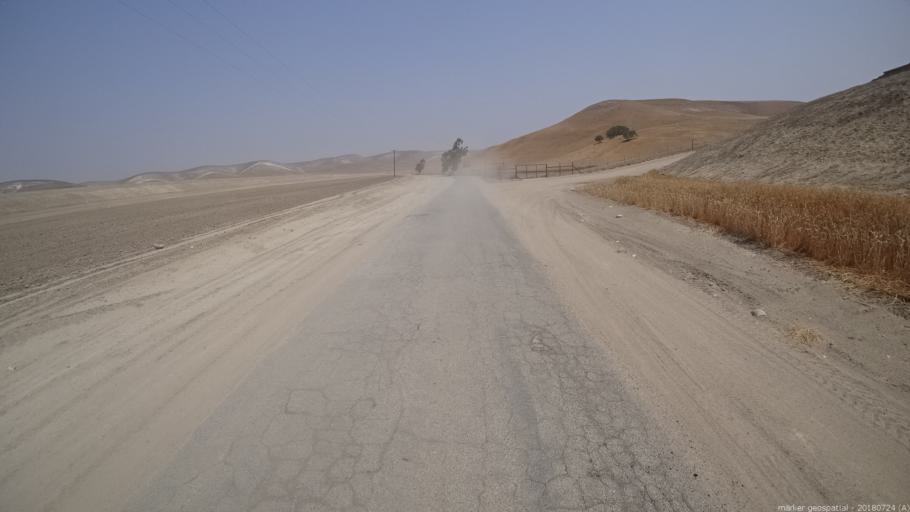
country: US
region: California
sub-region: Monterey County
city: King City
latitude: 36.1935
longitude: -121.0359
